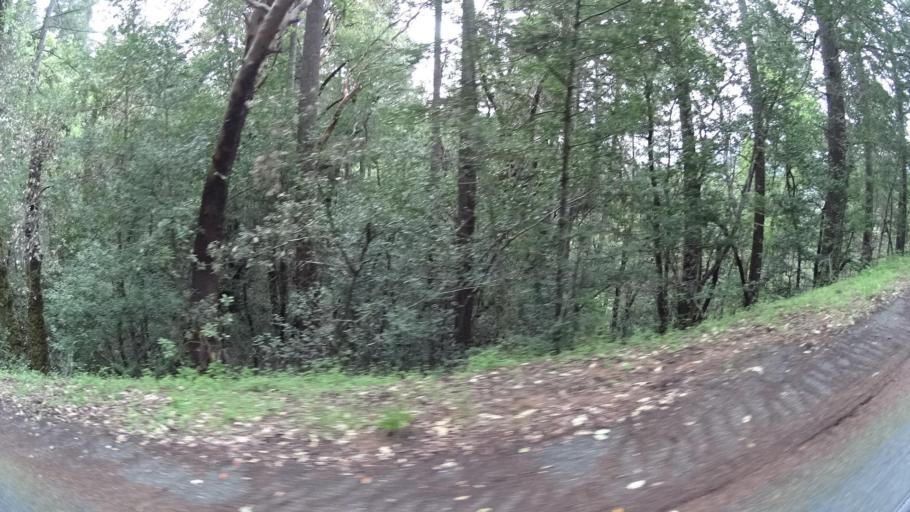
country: US
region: California
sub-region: Humboldt County
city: Willow Creek
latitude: 41.3653
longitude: -123.5040
